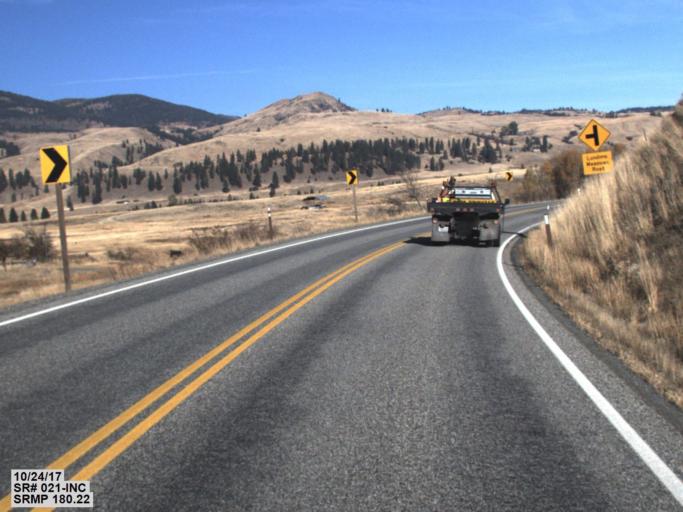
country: CA
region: British Columbia
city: Grand Forks
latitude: 48.8708
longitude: -118.6080
